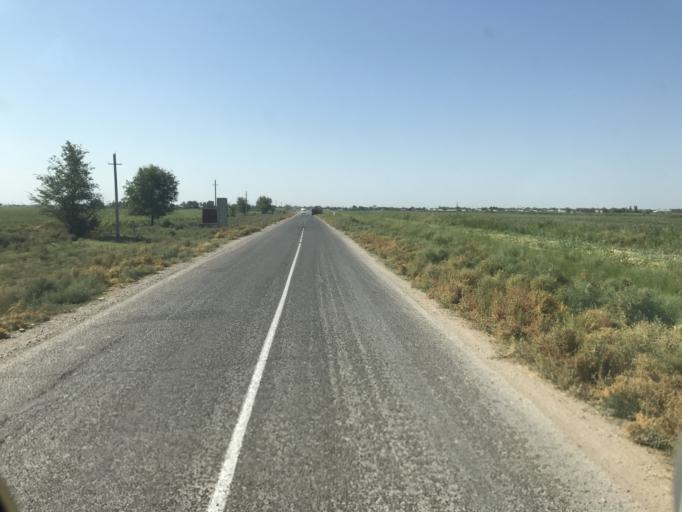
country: KZ
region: Ongtustik Qazaqstan
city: Myrzakent
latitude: 40.6822
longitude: 68.5566
